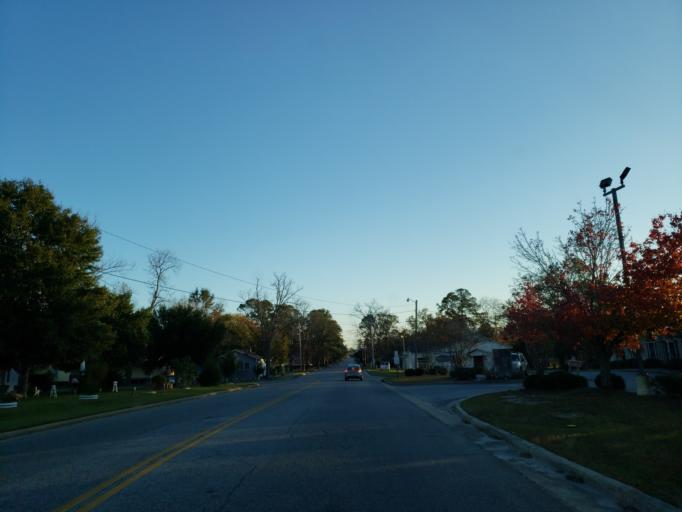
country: US
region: Georgia
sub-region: Crisp County
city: Cordele
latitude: 31.9632
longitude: -83.7795
